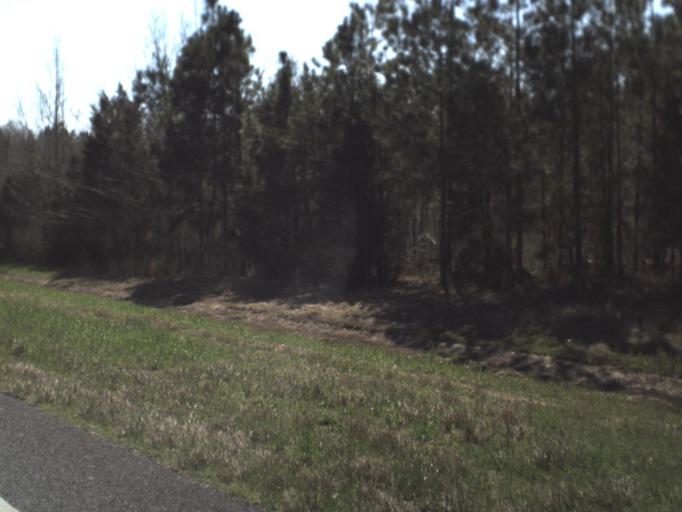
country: US
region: Florida
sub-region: Jackson County
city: Graceville
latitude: 30.8825
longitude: -85.3656
